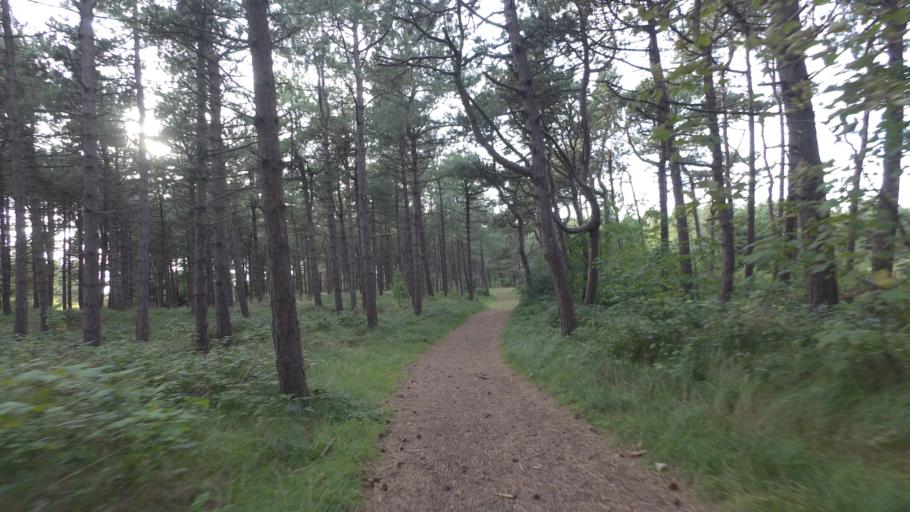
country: NL
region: Friesland
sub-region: Gemeente Ameland
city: Nes
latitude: 53.4587
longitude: 5.8196
